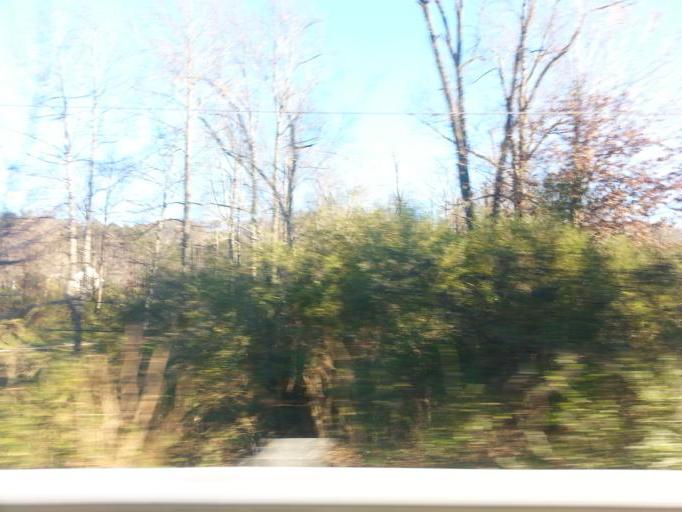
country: US
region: Tennessee
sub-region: Anderson County
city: Clinton
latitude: 36.1465
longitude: -84.1798
